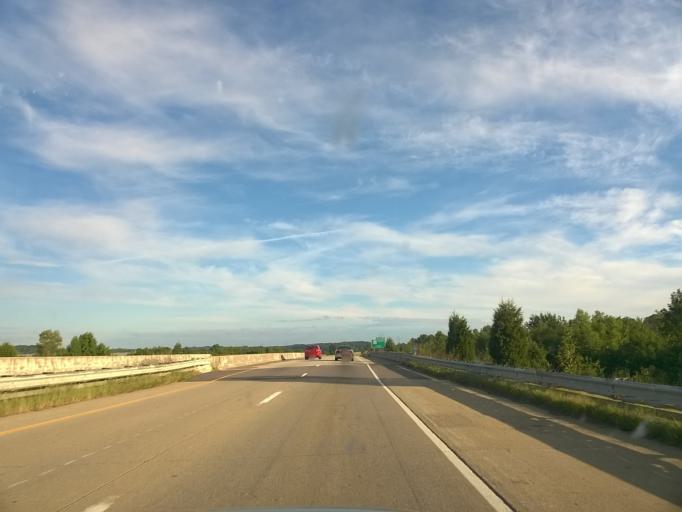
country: US
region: Indiana
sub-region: Vanderburgh County
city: Melody Hill
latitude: 38.1124
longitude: -87.4774
